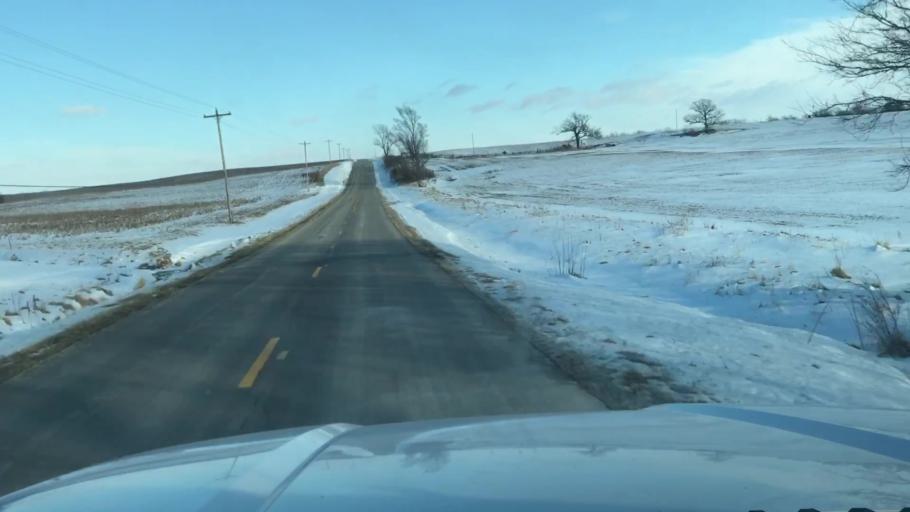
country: US
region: Missouri
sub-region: Holt County
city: Oregon
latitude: 40.1007
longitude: -95.0024
